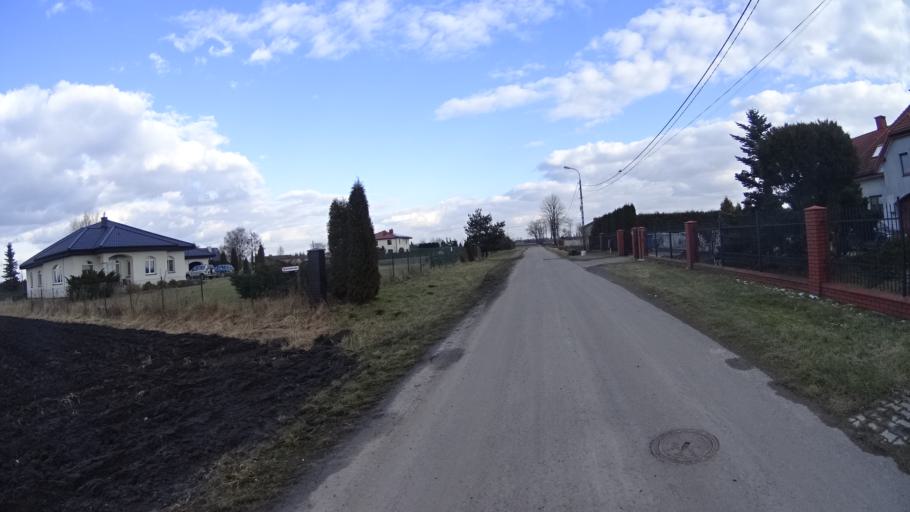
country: PL
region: Masovian Voivodeship
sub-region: Powiat warszawski zachodni
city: Ozarow Mazowiecki
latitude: 52.2455
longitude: 20.7908
